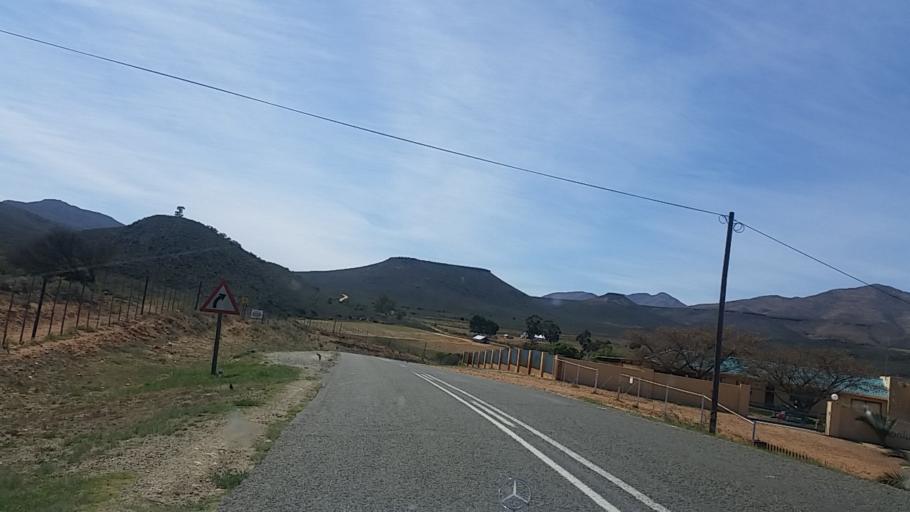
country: ZA
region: Western Cape
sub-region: Eden District Municipality
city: Knysna
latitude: -33.6423
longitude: 23.1352
